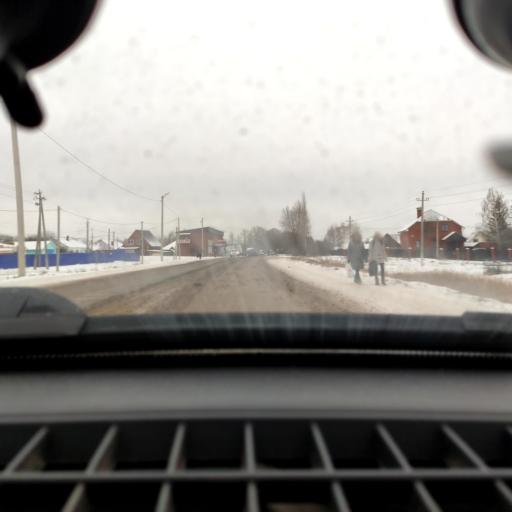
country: RU
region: Bashkortostan
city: Iglino
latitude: 54.8141
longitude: 56.4069
